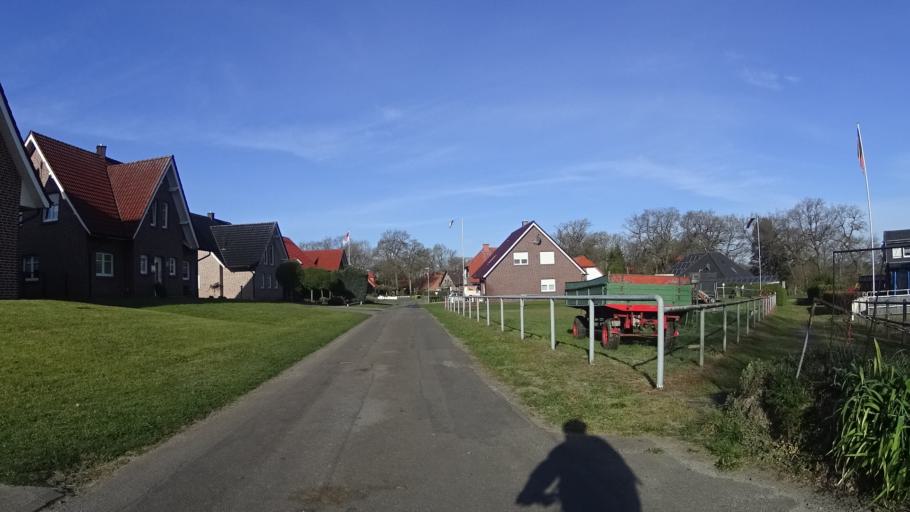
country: DE
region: Lower Saxony
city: Haren
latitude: 52.8130
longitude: 7.2595
